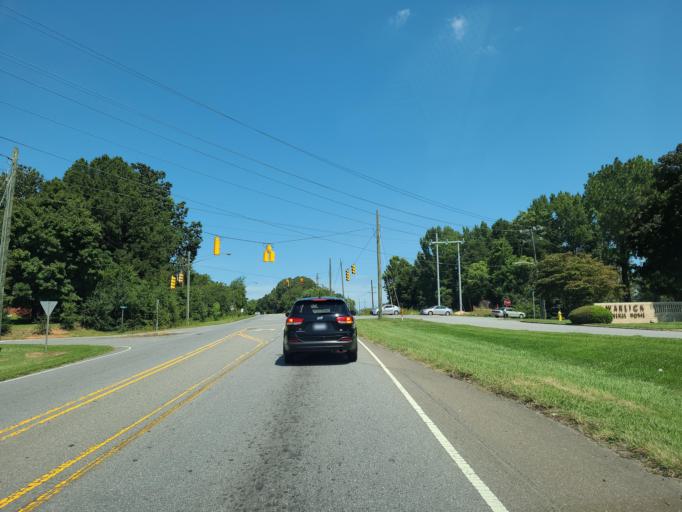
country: US
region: North Carolina
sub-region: Lincoln County
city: Lincolnton
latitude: 35.4716
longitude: -81.2393
